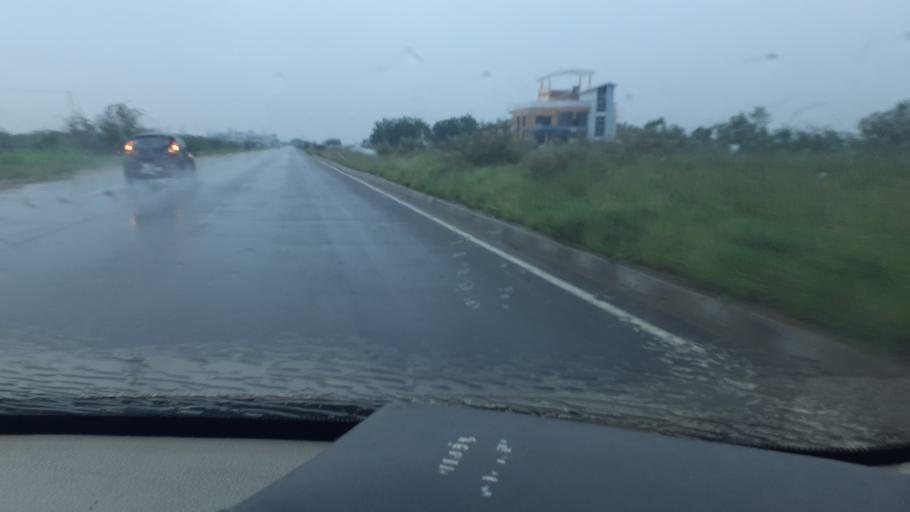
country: IN
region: Tamil Nadu
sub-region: Virudhunagar
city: Sattur
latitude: 9.4065
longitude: 77.9158
